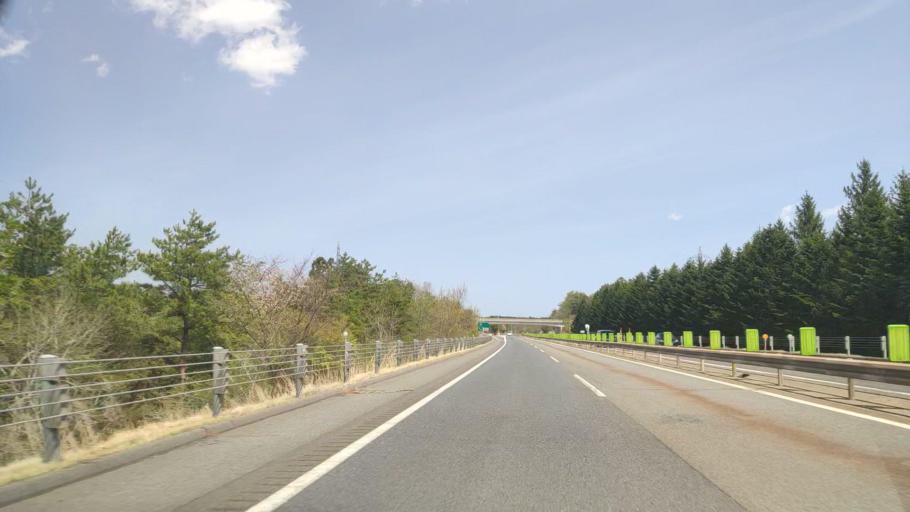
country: JP
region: Aomori
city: Hachinohe
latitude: 40.4395
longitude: 141.4480
